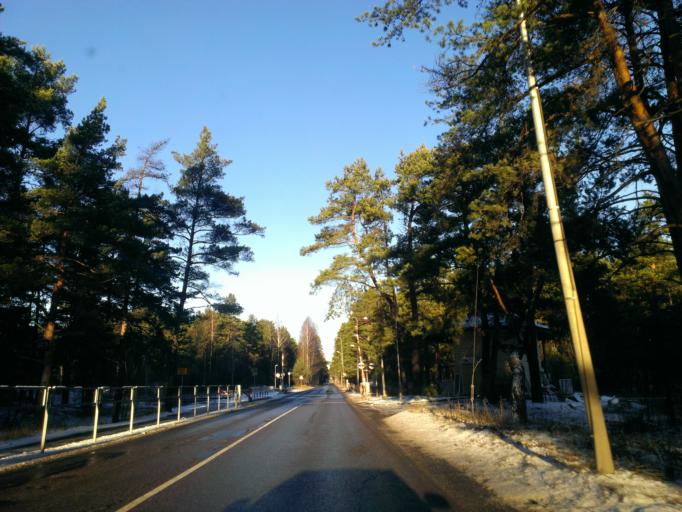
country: LV
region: Riga
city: Bolderaja
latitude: 57.0410
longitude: 24.1031
